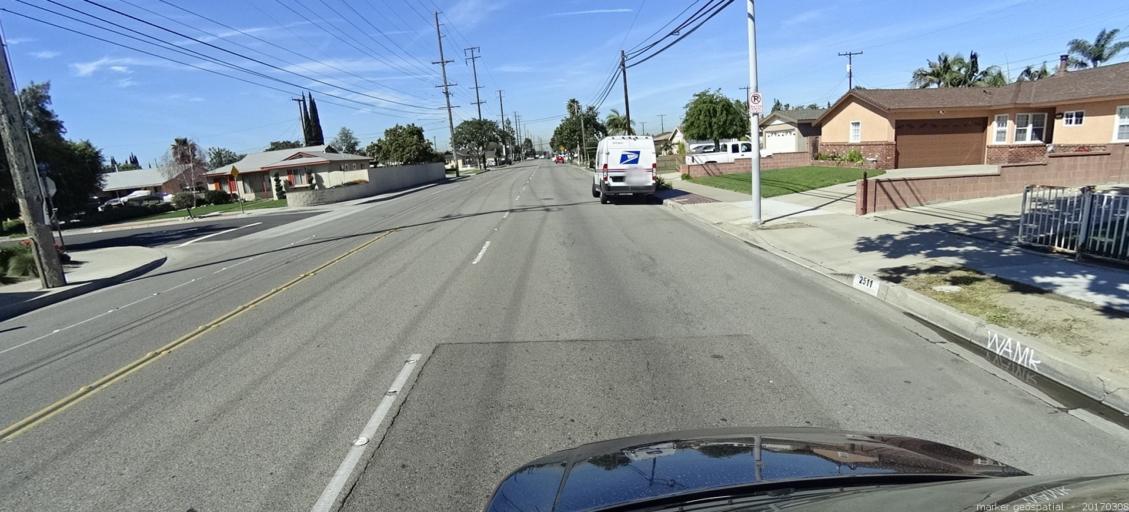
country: US
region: California
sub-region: Orange County
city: Buena Park
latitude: 33.8396
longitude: -117.9724
